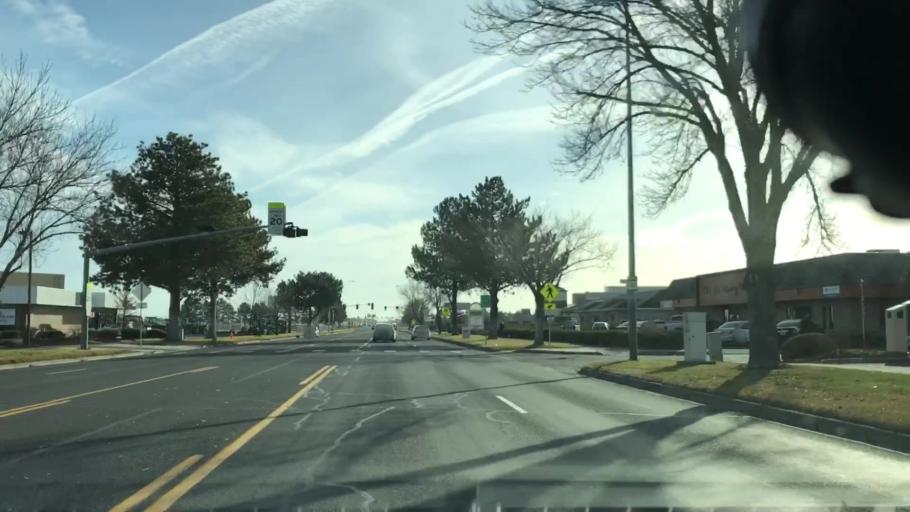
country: US
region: Washington
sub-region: Grant County
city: Moses Lake
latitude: 47.1148
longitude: -119.2622
